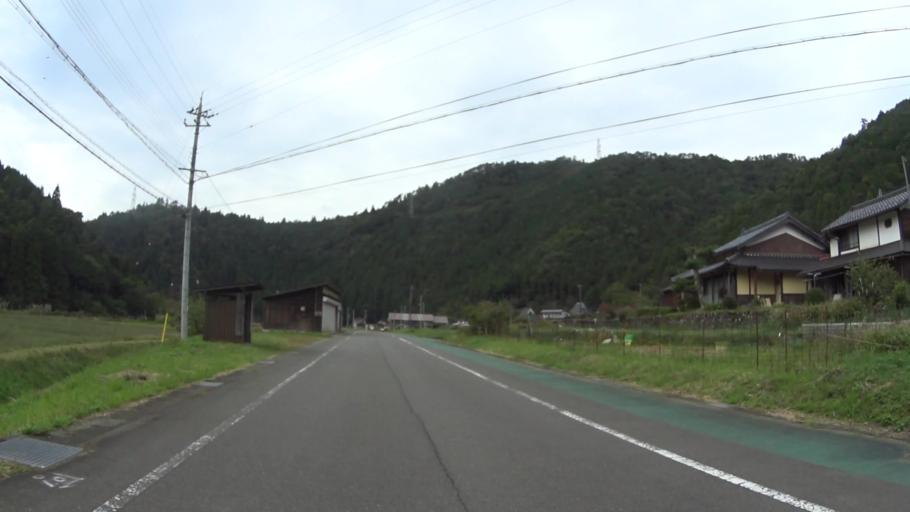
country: JP
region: Fukui
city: Obama
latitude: 35.3198
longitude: 135.6576
